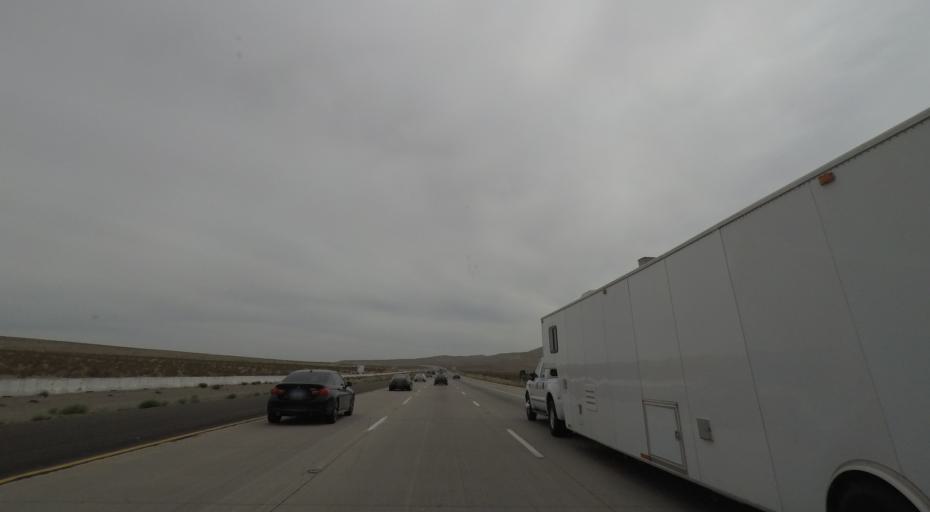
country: US
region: California
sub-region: San Bernardino County
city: Lenwood
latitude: 34.7161
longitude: -117.1983
